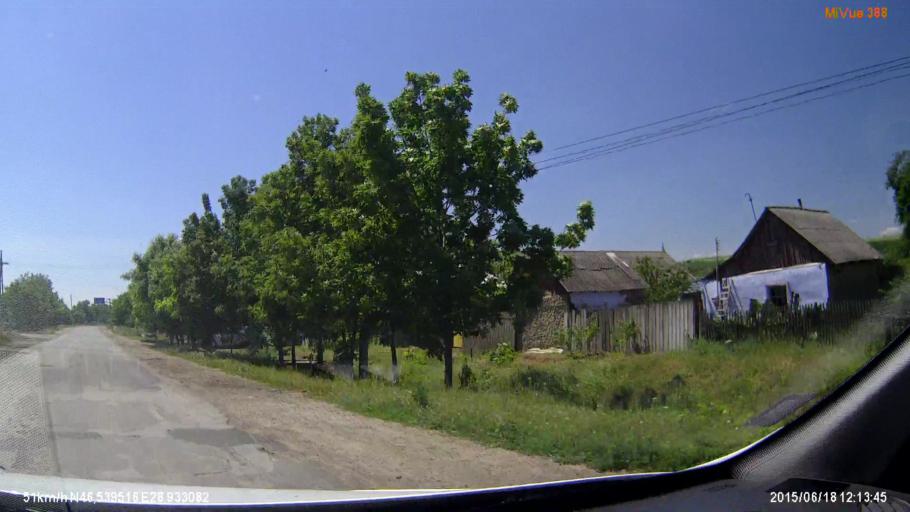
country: MD
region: Cimislia
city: Cimislia
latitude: 46.5398
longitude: 28.9330
